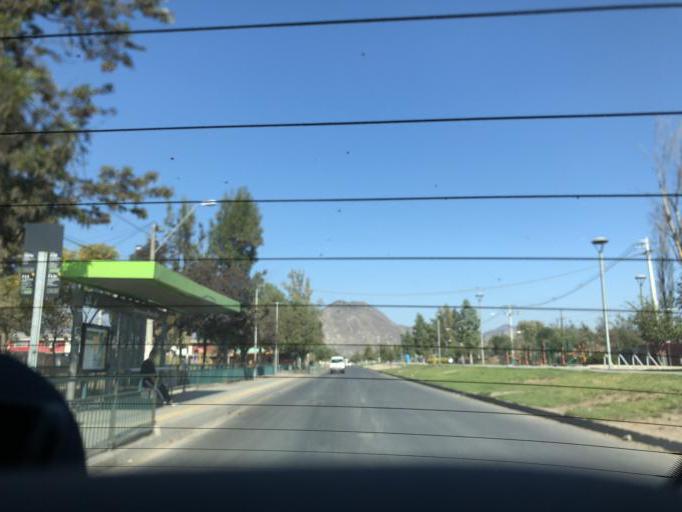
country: CL
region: Santiago Metropolitan
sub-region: Provincia de Santiago
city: La Pintana
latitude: -33.6274
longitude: -70.6284
